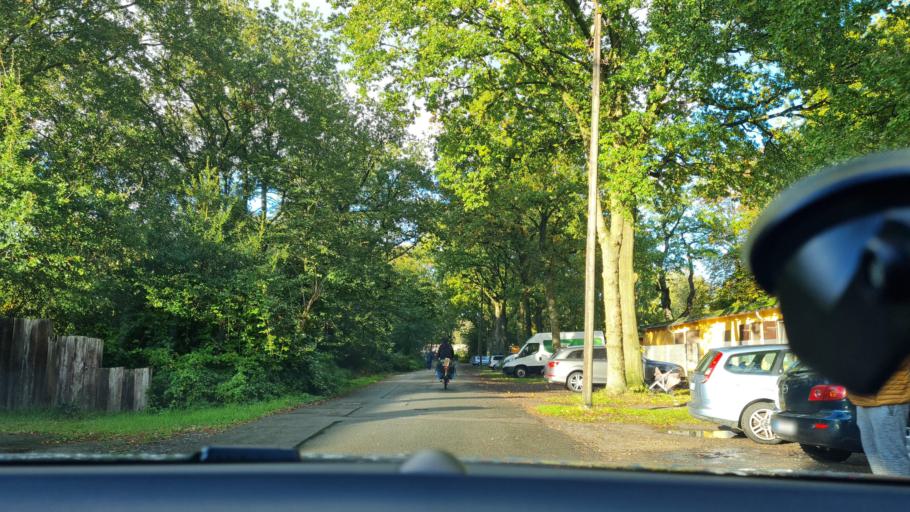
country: DE
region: North Rhine-Westphalia
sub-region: Regierungsbezirk Dusseldorf
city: Dinslaken
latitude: 51.5521
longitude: 6.7547
